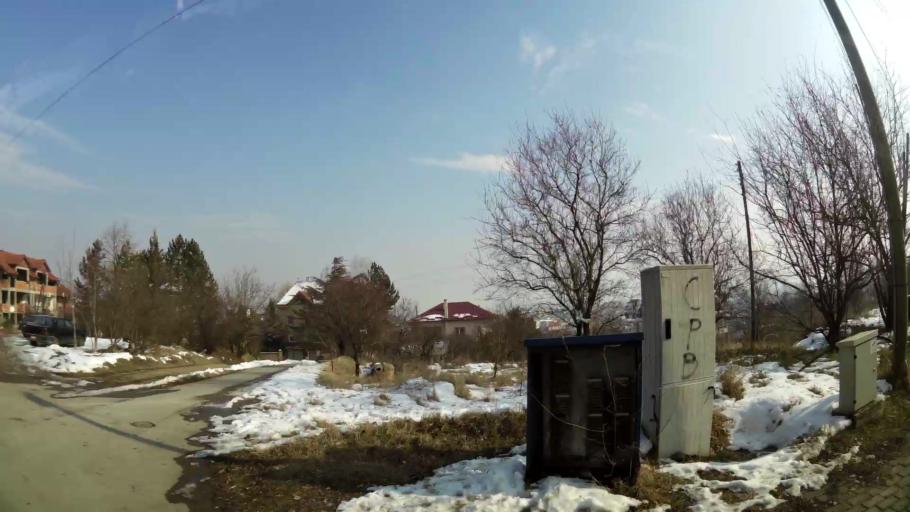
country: MK
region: Suto Orizari
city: Suto Orizare
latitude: 42.0279
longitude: 21.3788
